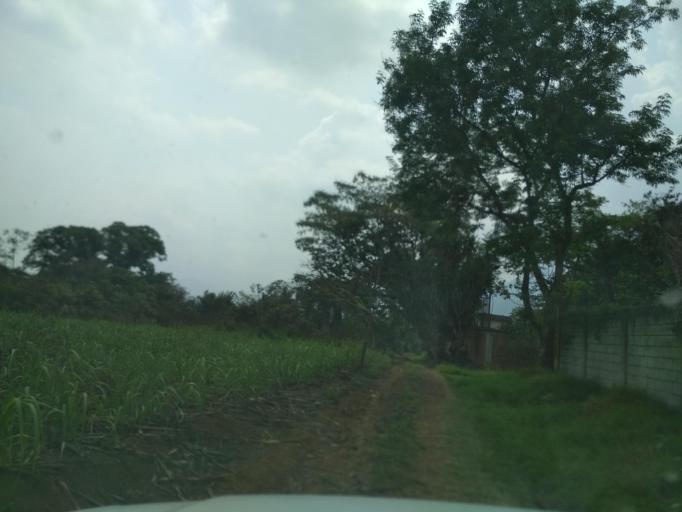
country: MX
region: Veracruz
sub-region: Cordoba
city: San Jose de Tapia
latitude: 18.8523
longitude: -96.9783
